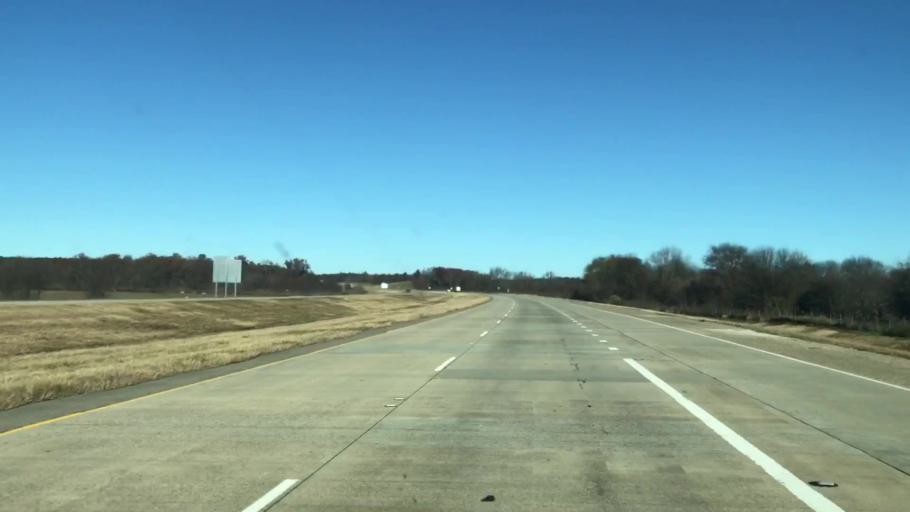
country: US
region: Louisiana
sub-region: Caddo Parish
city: Vivian
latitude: 32.9035
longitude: -93.8643
